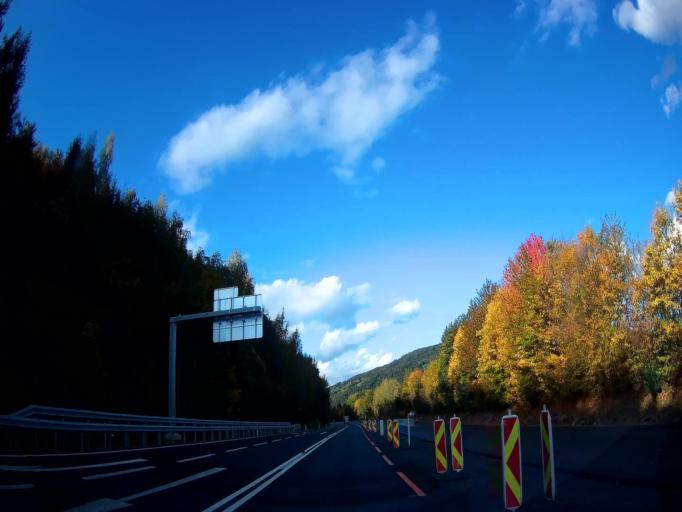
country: AT
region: Carinthia
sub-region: Politischer Bezirk Wolfsberg
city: Wolfsberg
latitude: 46.8521
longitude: 14.8353
